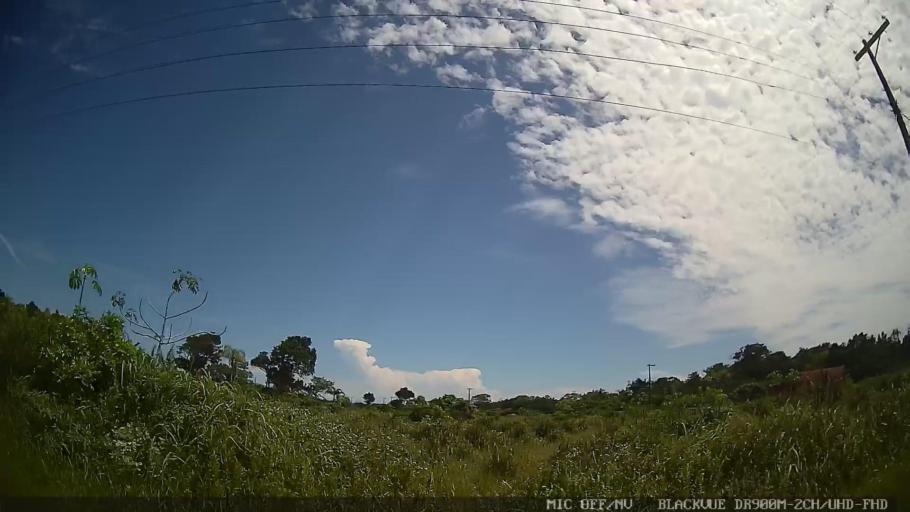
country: BR
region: Sao Paulo
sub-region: Iguape
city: Iguape
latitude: -24.7133
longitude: -47.5083
